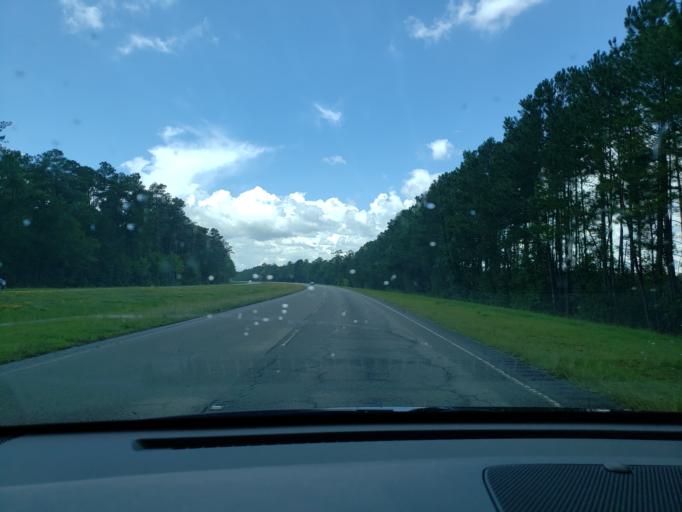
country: US
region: North Carolina
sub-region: Bladen County
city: Elizabethtown
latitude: 34.6324
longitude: -78.6568
